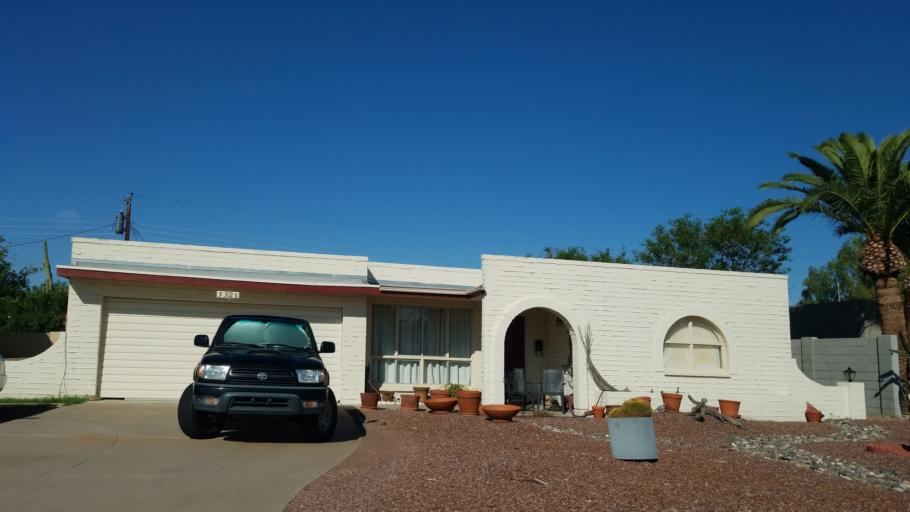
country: US
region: Arizona
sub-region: Maricopa County
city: Scottsdale
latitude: 33.5146
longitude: -111.9003
